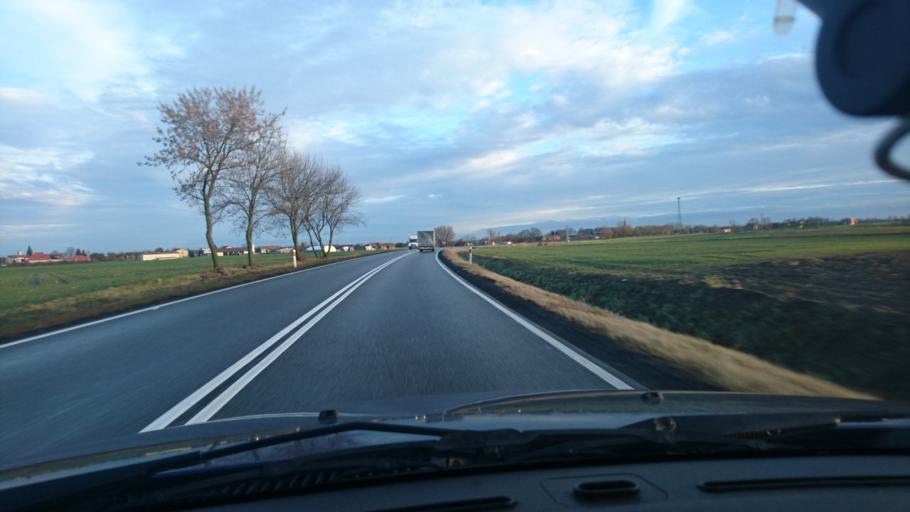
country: PL
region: Greater Poland Voivodeship
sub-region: Powiat kepinski
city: Opatow
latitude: 51.2207
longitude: 18.1338
